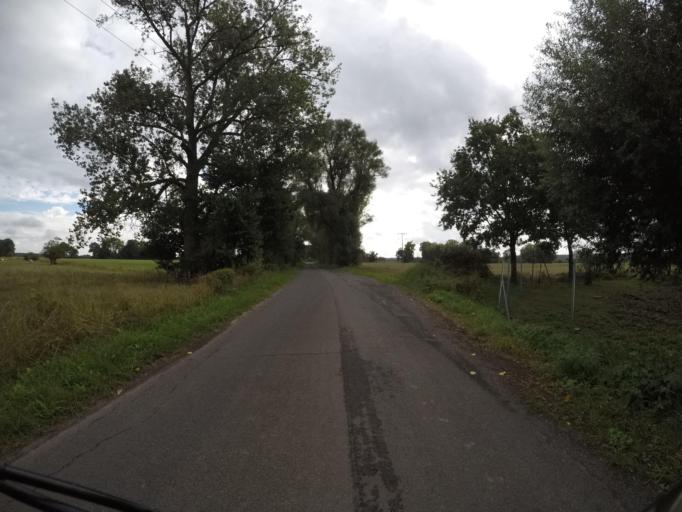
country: DE
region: Lower Saxony
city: Tosterglope
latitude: 53.2715
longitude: 10.8328
